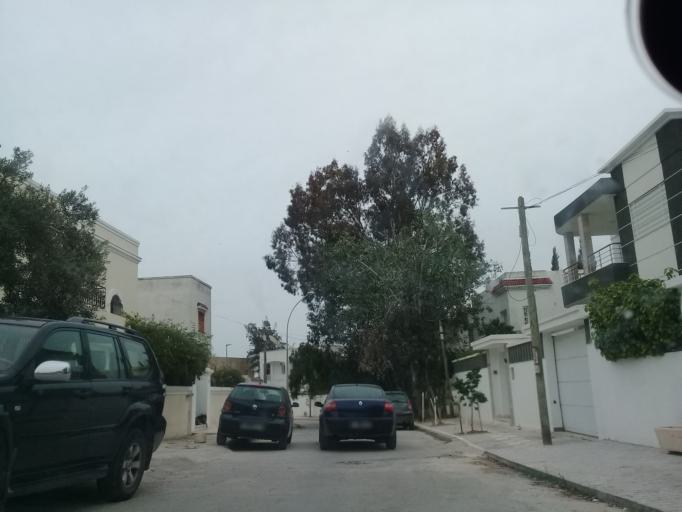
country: TN
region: Tunis
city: Tunis
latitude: 36.8431
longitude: 10.1516
